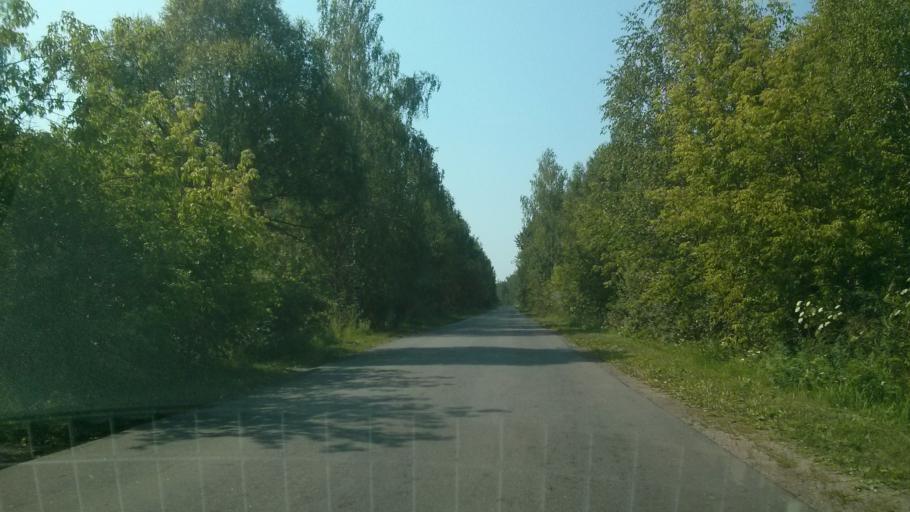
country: RU
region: Vladimir
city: Murom
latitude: 55.5237
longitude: 42.0221
